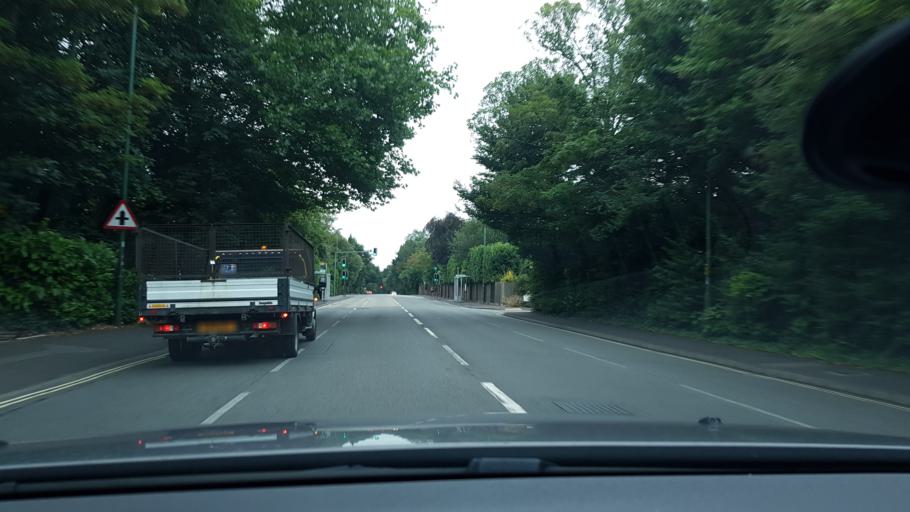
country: GB
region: England
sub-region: Southampton
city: Southampton
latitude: 50.9401
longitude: -1.4068
